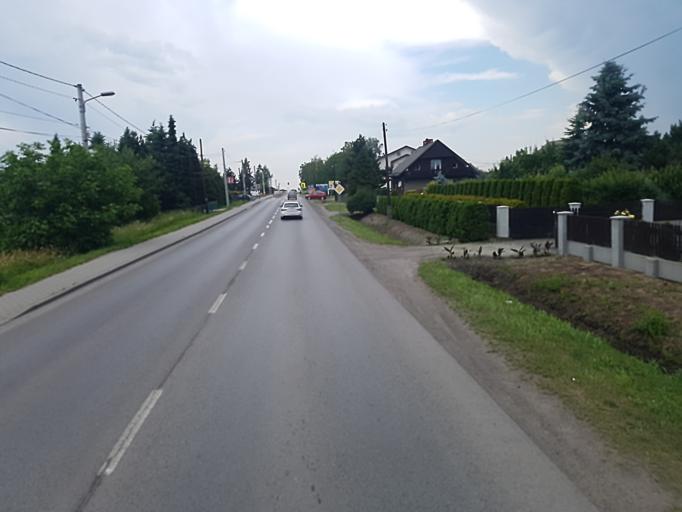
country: PL
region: Silesian Voivodeship
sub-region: Powiat wodzislawski
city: Wodzislaw Slaski
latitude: 49.9893
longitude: 18.4974
